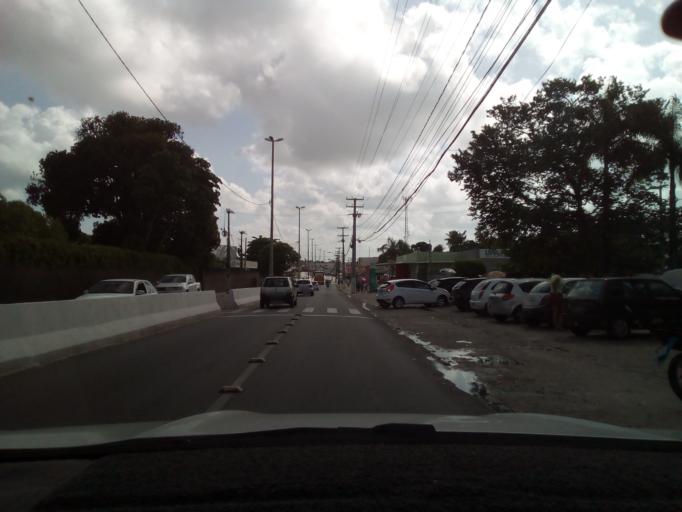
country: BR
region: Paraiba
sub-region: Bayeux
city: Bayeux
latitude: -7.1254
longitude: -34.9265
